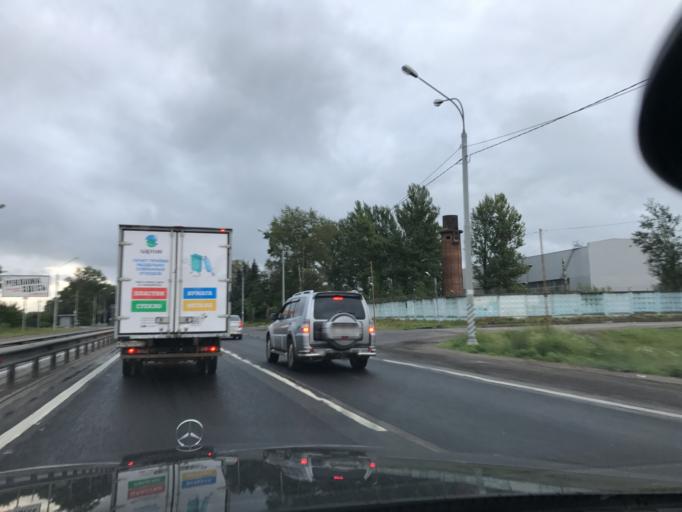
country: RU
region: Moskovskaya
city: Pavlovskiy Posad
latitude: 55.8522
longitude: 38.6240
